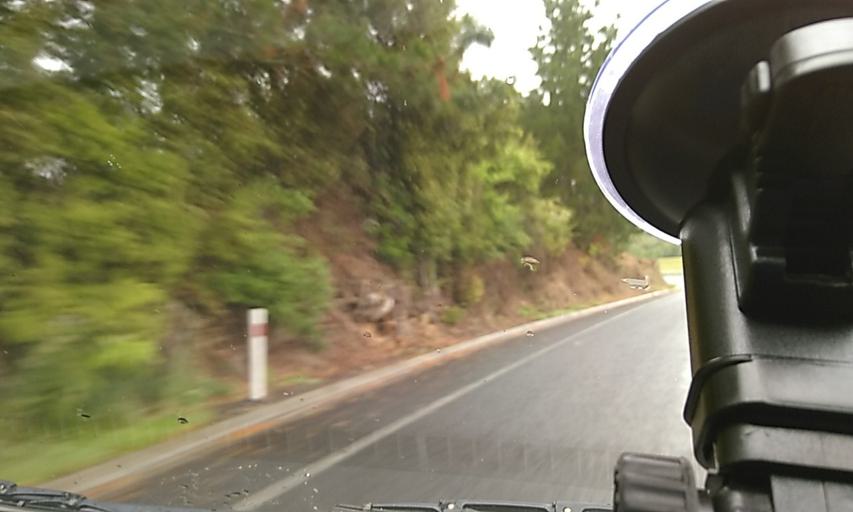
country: NZ
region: Auckland
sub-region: Auckland
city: Pukekohe East
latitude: -37.3132
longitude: 174.9377
